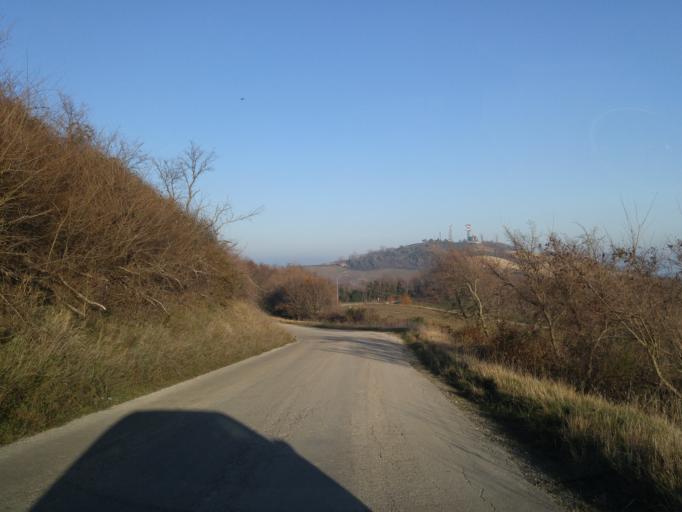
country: IT
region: The Marches
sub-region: Provincia di Pesaro e Urbino
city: Mombaroccio
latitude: 43.7778
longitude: 12.8359
